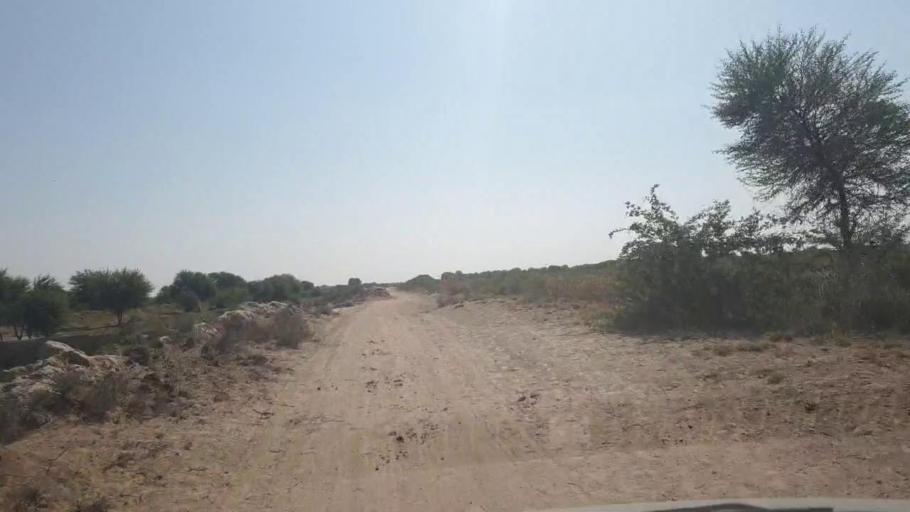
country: PK
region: Sindh
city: Digri
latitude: 24.9327
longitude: 69.1638
